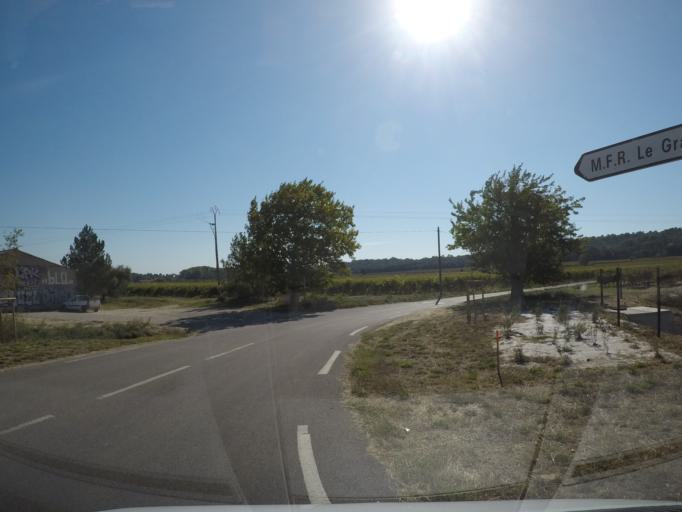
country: FR
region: Languedoc-Roussillon
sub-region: Departement du Gard
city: Uzes
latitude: 43.9939
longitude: 4.3923
